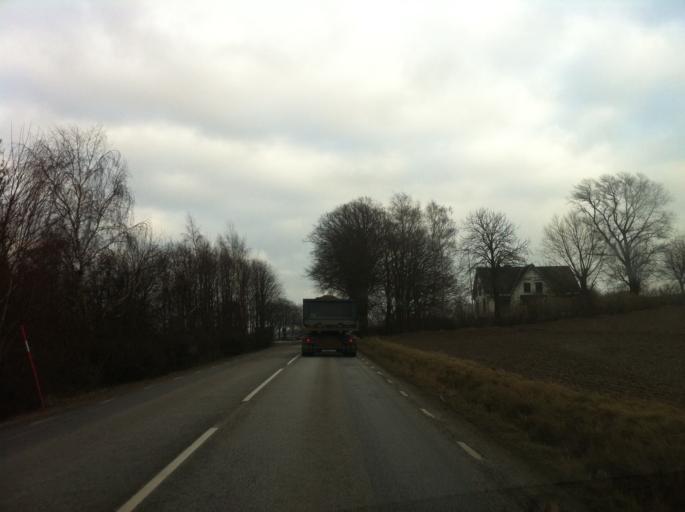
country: SE
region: Skane
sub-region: Kavlinge Kommun
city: Loddekopinge
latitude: 55.8185
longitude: 13.0347
